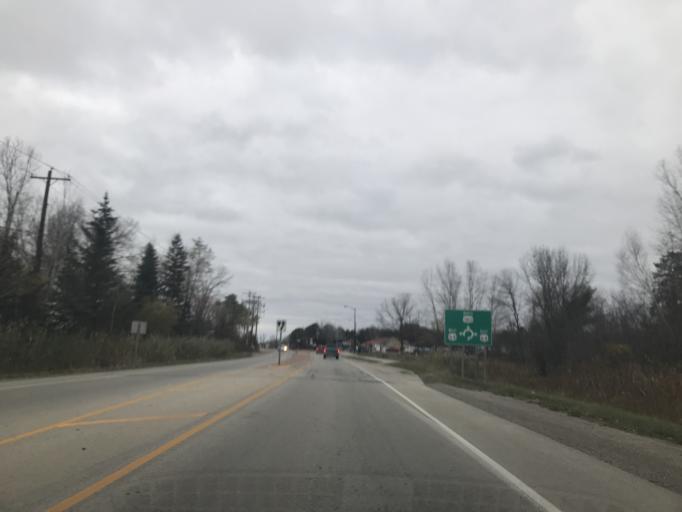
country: US
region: Wisconsin
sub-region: Marinette County
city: Marinette
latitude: 45.0982
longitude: -87.6604
